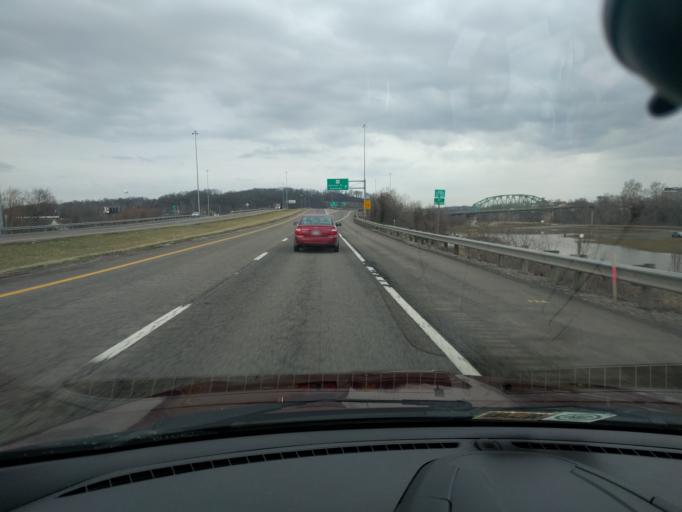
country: US
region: West Virginia
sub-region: Wood County
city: Parkersburg
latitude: 39.2571
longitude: -81.5506
